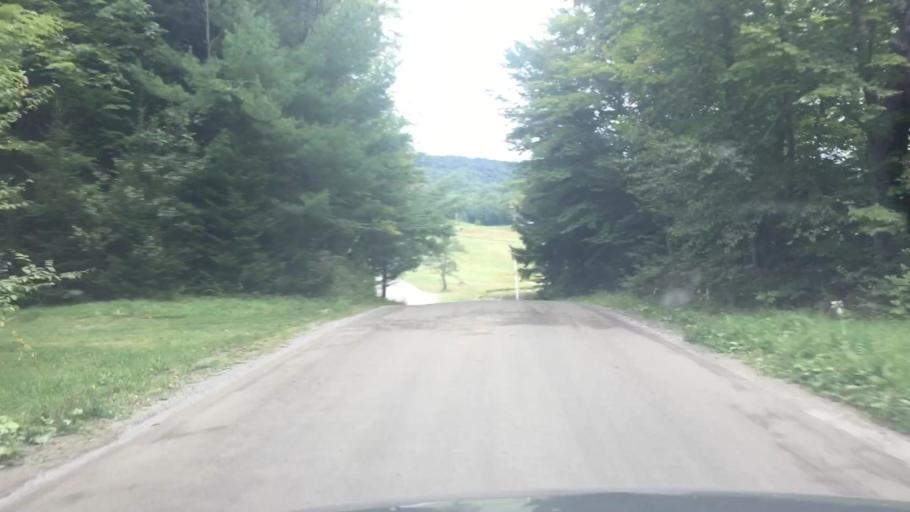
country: US
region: Vermont
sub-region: Windham County
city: Dover
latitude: 42.8302
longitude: -72.7989
